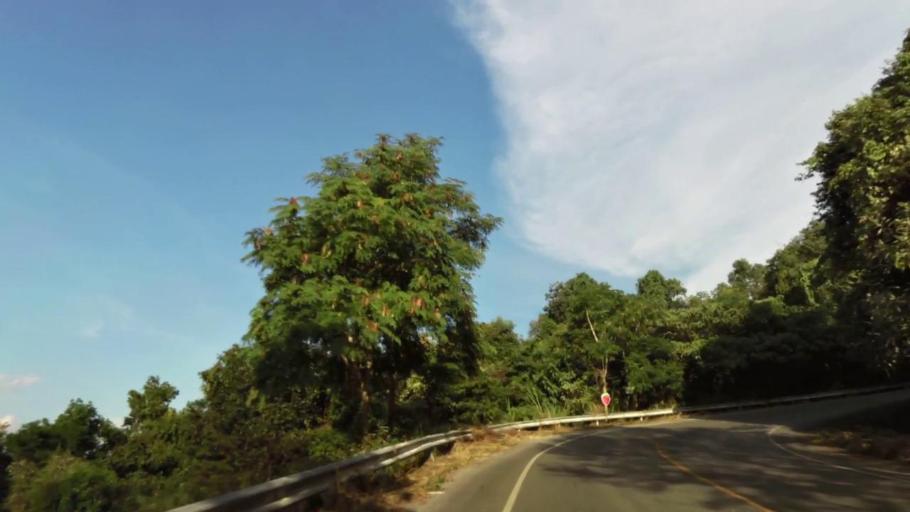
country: TH
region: Chiang Rai
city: Khun Tan
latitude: 19.8617
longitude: 100.4311
